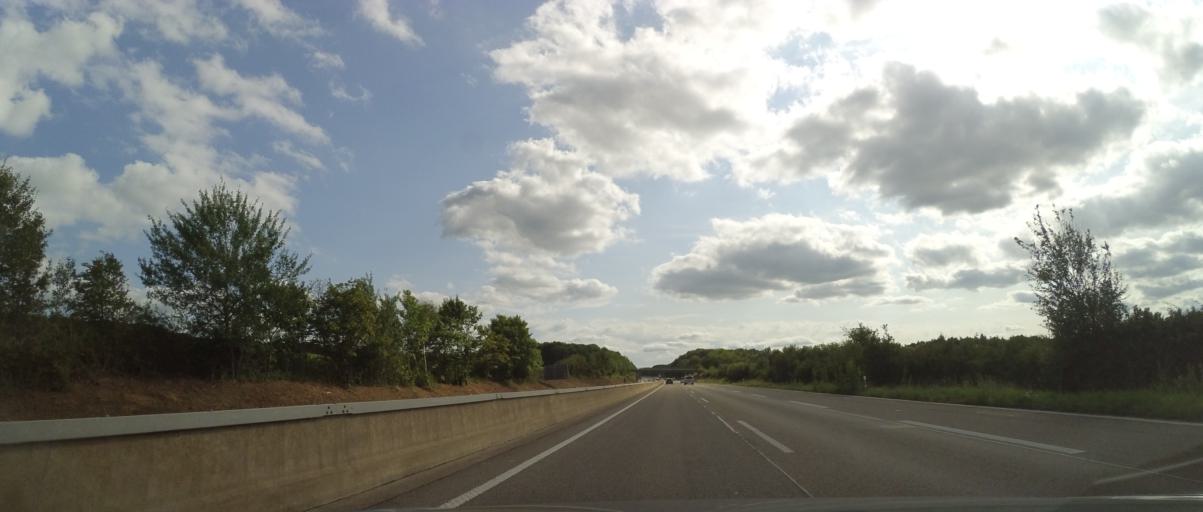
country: DE
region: North Rhine-Westphalia
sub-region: Regierungsbezirk Koln
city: Mechernich
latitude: 50.5716
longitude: 6.6848
